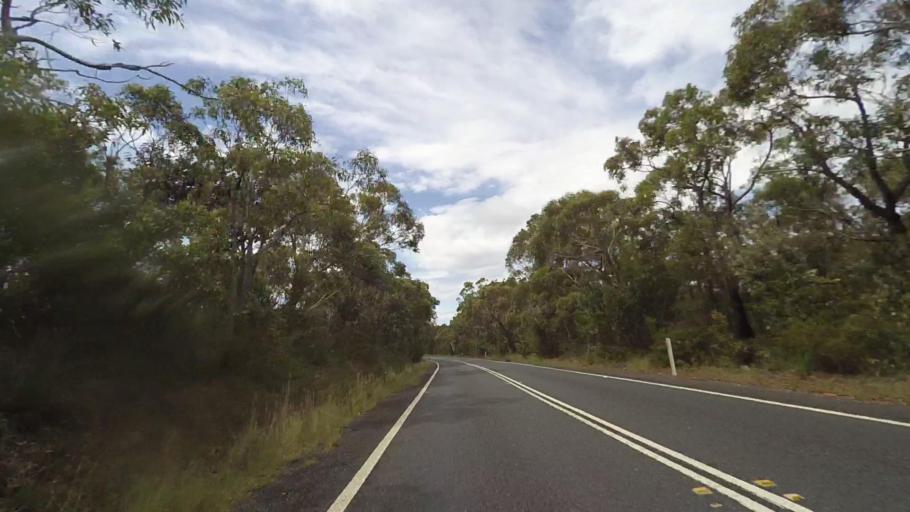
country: AU
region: New South Wales
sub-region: Sutherland Shire
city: Grays Point
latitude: -34.0936
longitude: 151.0626
